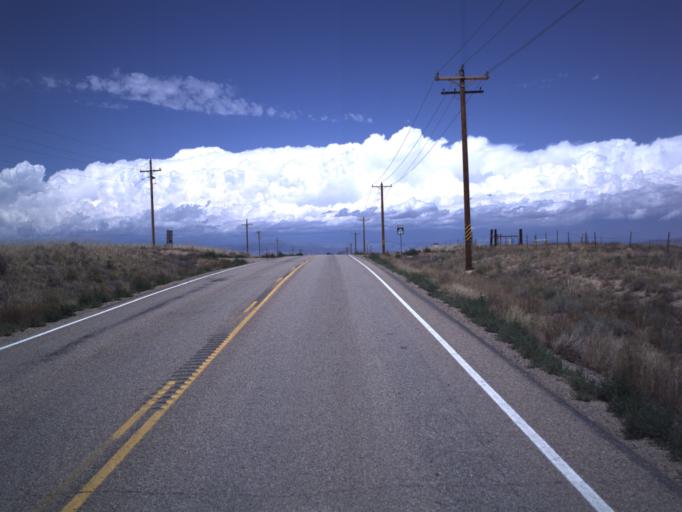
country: US
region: Utah
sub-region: Uintah County
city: Naples
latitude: 40.1545
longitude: -109.6642
